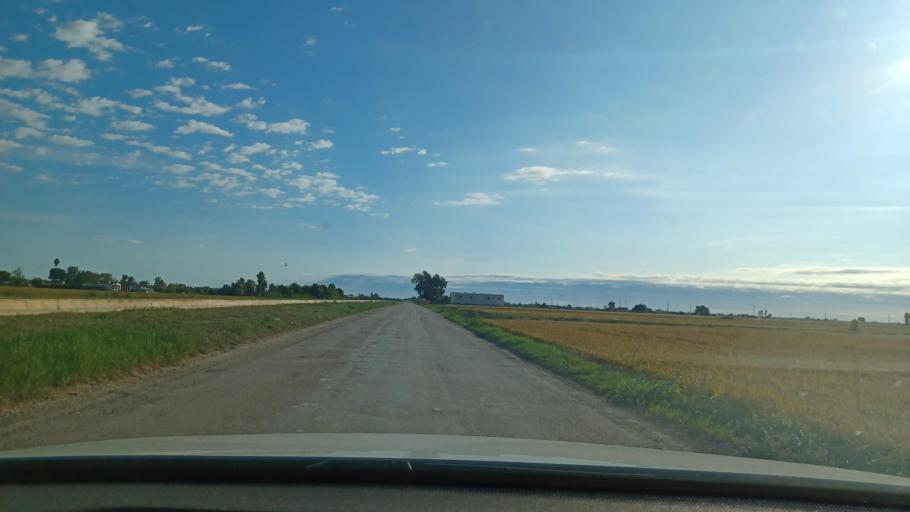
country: ES
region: Catalonia
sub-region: Provincia de Tarragona
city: Amposta
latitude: 40.7006
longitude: 0.6210
